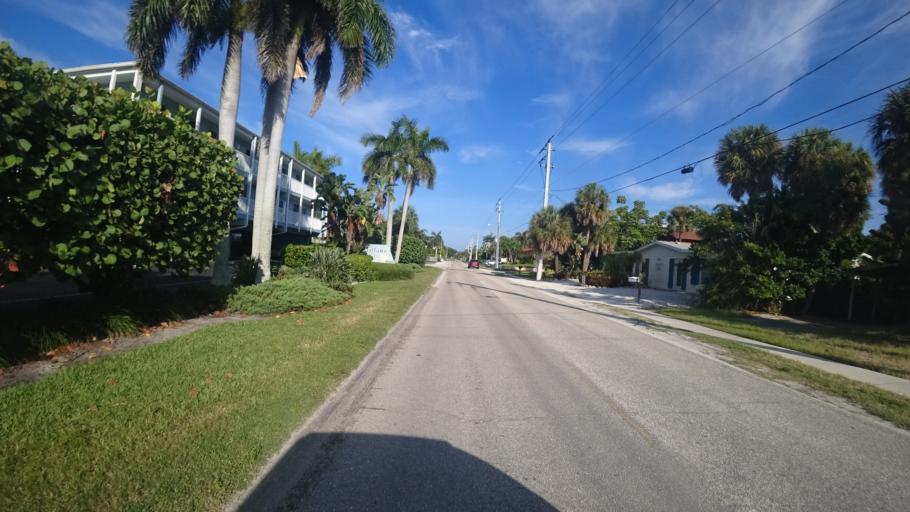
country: US
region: Florida
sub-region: Manatee County
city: Anna Maria
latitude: 27.5145
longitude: -82.7235
